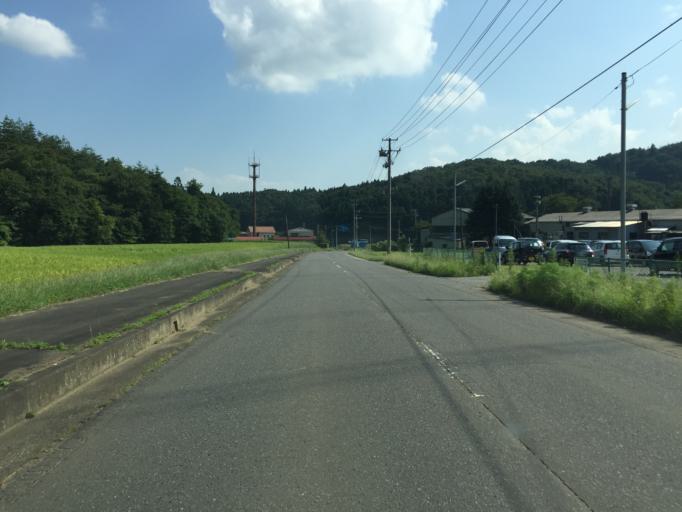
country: JP
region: Fukushima
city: Nihommatsu
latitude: 37.5993
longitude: 140.4004
